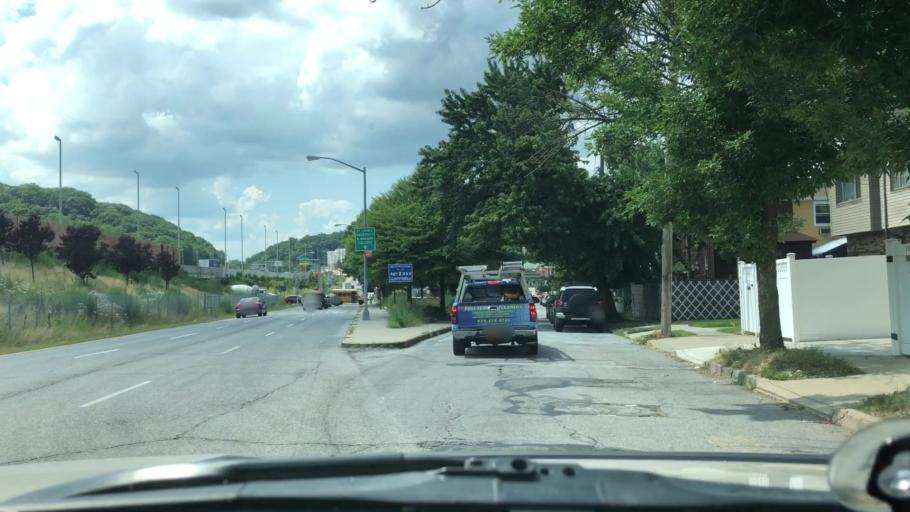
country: US
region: New Jersey
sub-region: Hudson County
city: Bayonne
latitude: 40.6082
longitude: -74.0868
